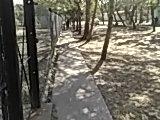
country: AR
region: Chaco
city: Presidencia Roque Saenz Pena
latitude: -26.8190
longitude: -60.4180
